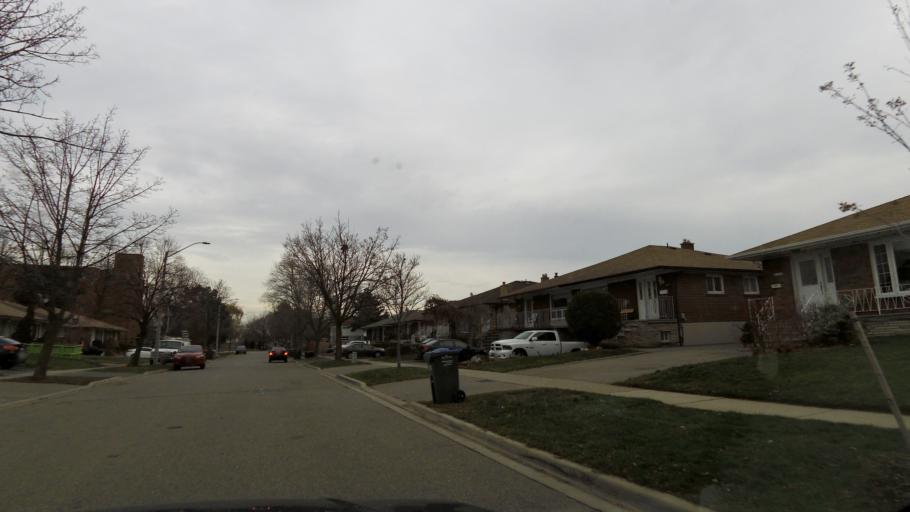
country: CA
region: Ontario
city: Etobicoke
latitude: 43.6208
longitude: -79.5870
